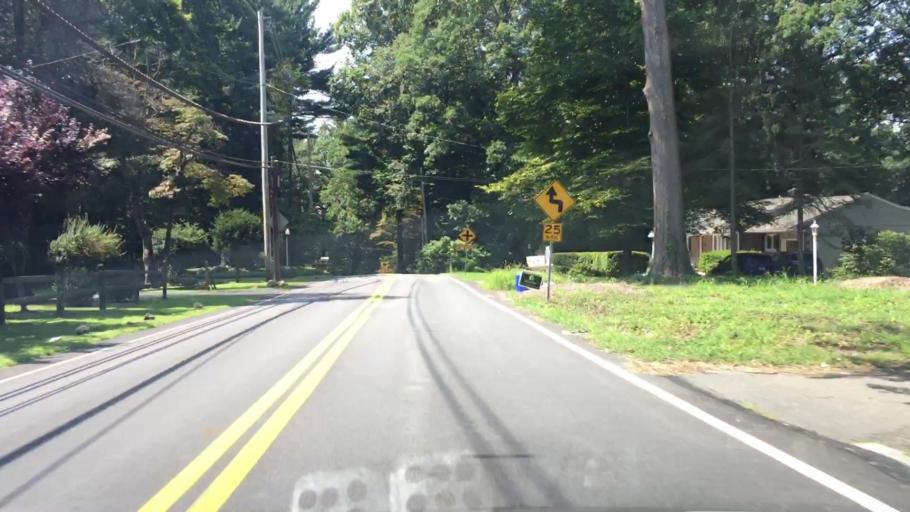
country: US
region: Pennsylvania
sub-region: Delaware County
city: Lima
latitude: 39.9016
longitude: -75.4196
